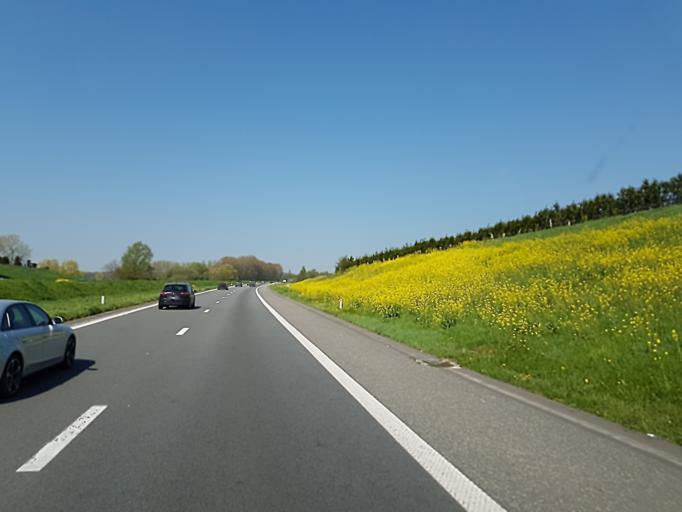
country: BE
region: Flanders
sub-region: Provincie West-Vlaanderen
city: Zonnebeke
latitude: 50.8417
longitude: 2.9921
